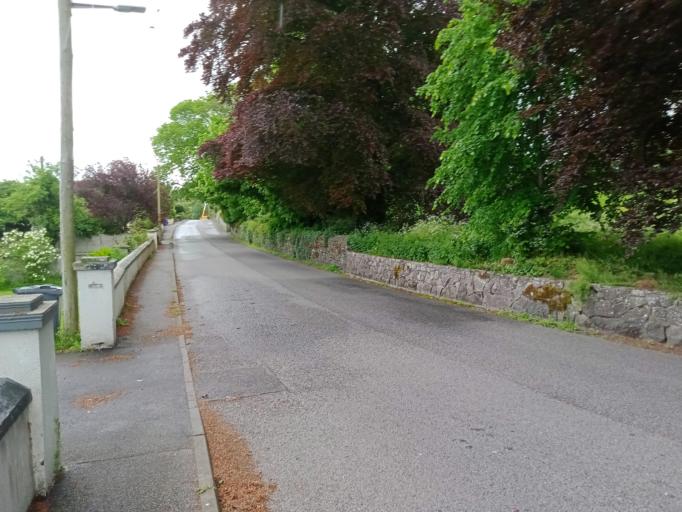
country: IE
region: Leinster
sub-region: Kilkenny
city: Thomastown
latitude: 52.5212
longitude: -7.1354
